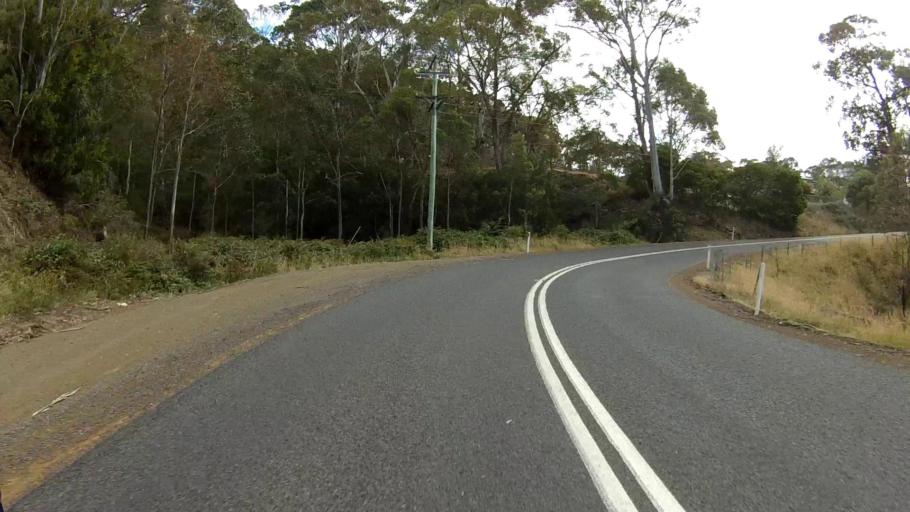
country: AU
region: Tasmania
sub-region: Clarence
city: Lindisfarne
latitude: -42.7823
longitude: 147.3594
